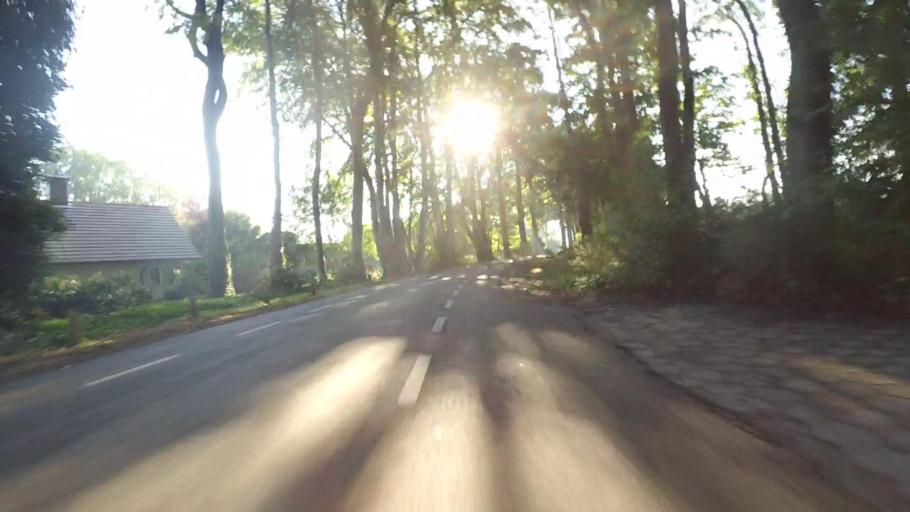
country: NL
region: Gelderland
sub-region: Gemeente Epe
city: Vaassen
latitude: 52.2900
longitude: 5.9426
